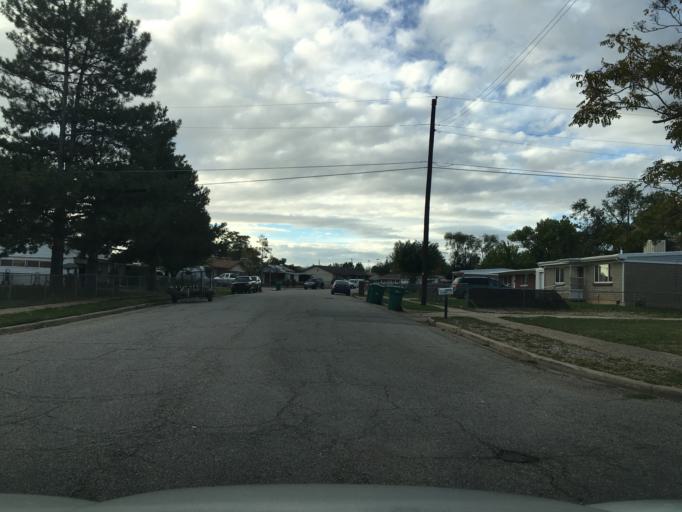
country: US
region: Utah
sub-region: Davis County
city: Layton
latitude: 41.0805
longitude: -111.9937
